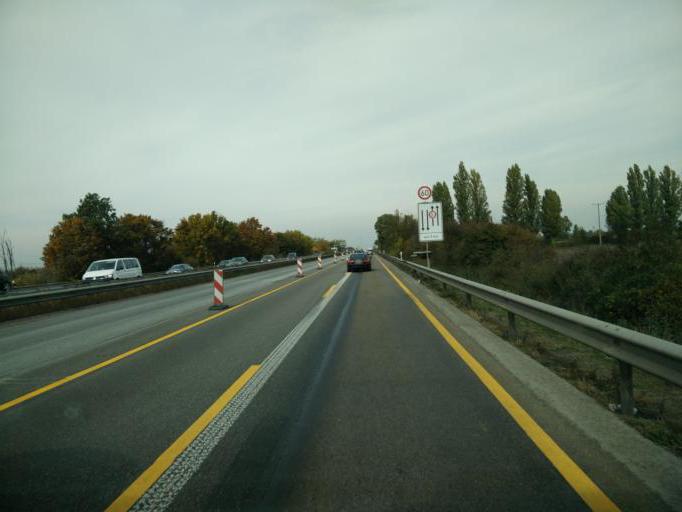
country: DE
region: Rheinland-Pfalz
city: Maxdorf
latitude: 49.4960
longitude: 8.3119
